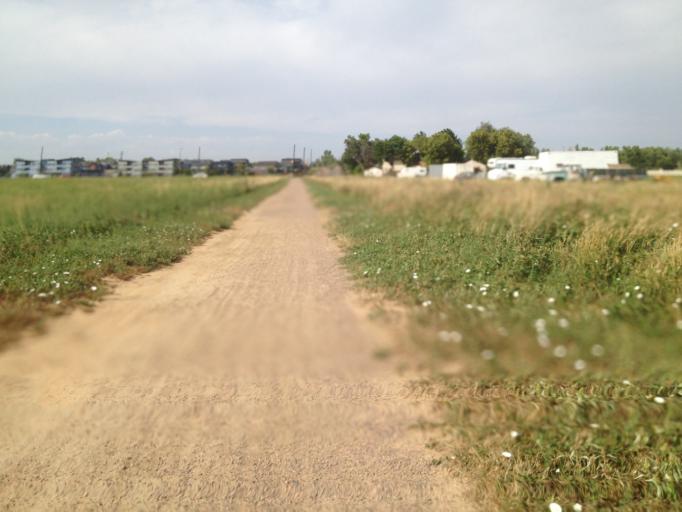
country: US
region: Colorado
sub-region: Boulder County
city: Louisville
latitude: 39.9848
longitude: -105.1188
